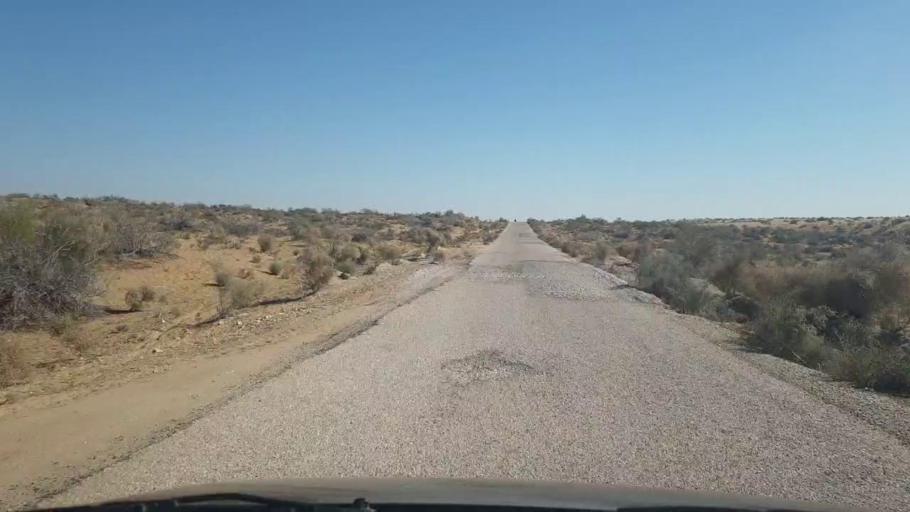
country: PK
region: Sindh
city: Bozdar
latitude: 26.9995
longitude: 68.8531
